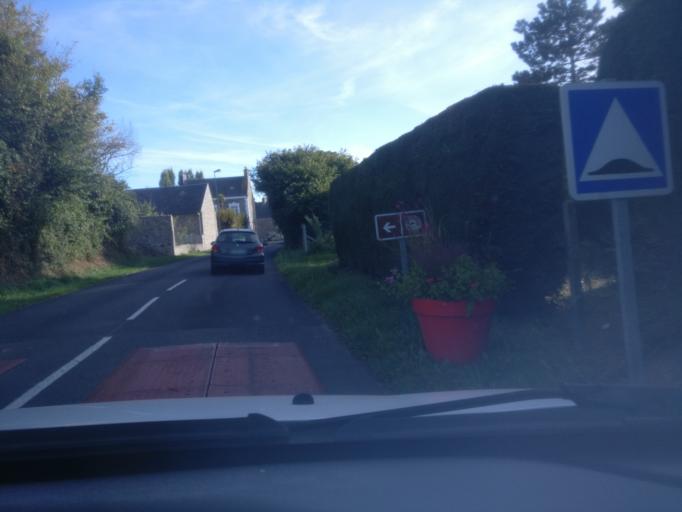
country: FR
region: Lower Normandy
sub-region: Departement de la Manche
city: Sartilly
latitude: 48.7135
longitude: -1.4994
